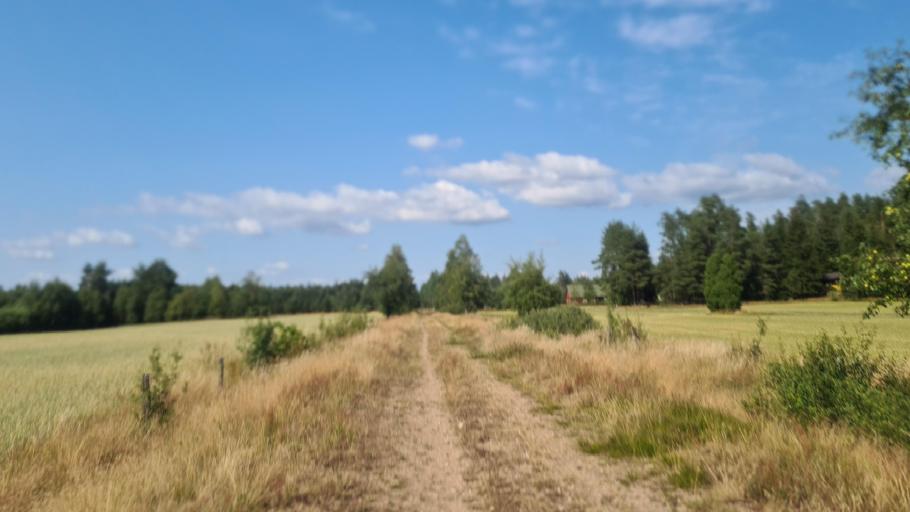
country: SE
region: Kronoberg
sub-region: Ljungby Kommun
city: Ljungby
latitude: 56.7576
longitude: 13.8879
